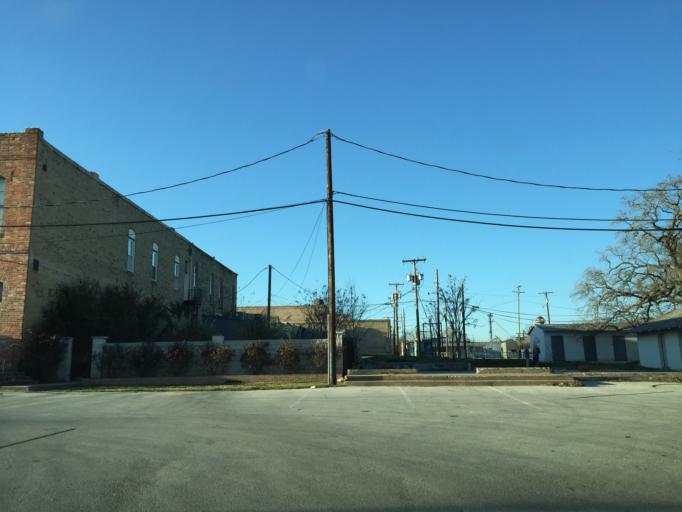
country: US
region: Texas
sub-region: Bastrop County
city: Elgin
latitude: 30.3477
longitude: -97.3699
